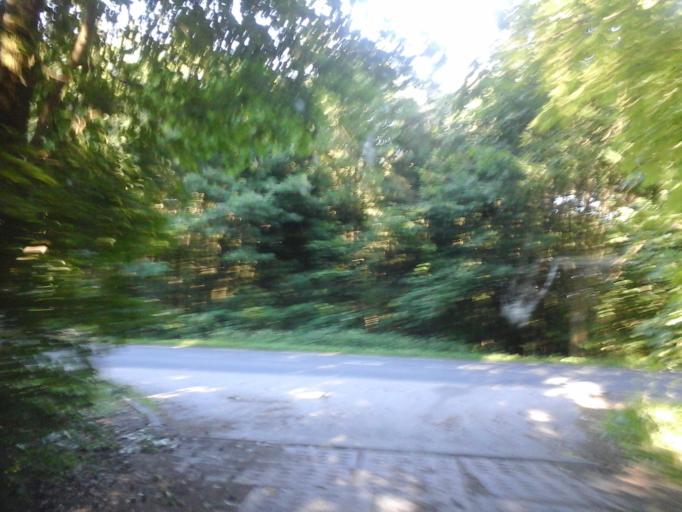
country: PL
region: West Pomeranian Voivodeship
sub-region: Powiat stargardzki
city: Chociwel
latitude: 53.5074
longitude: 15.3348
